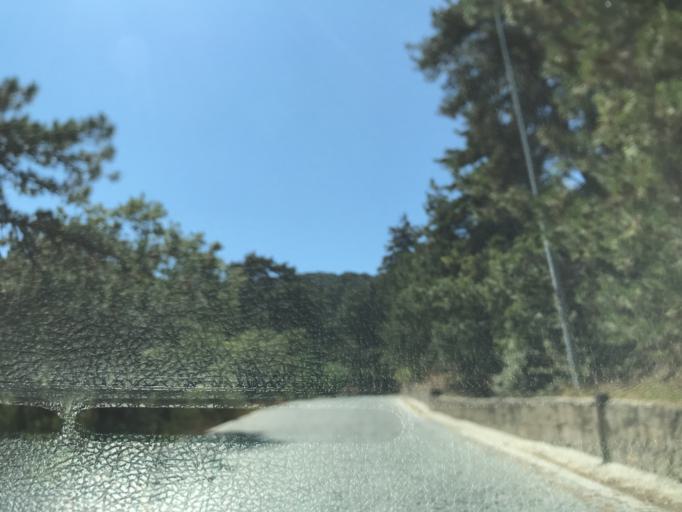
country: TR
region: Yozgat
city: Yozgat
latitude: 39.8059
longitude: 34.8091
